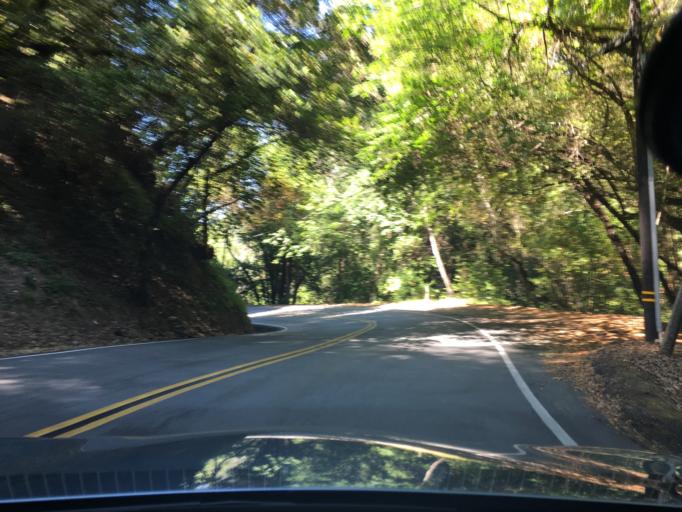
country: US
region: California
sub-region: Santa Clara County
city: Lexington Hills
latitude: 37.1692
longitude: -121.9851
